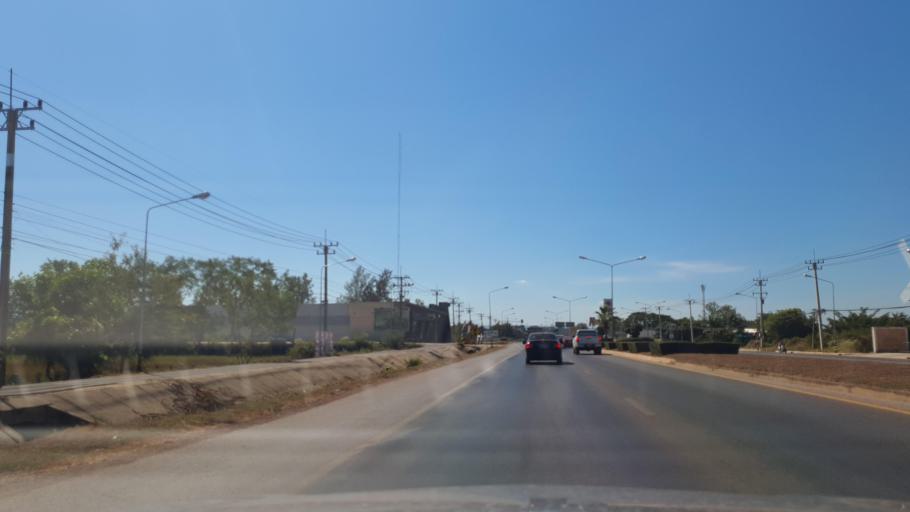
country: TH
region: Sakon Nakhon
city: Sakon Nakhon
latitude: 17.2073
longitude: 104.1014
